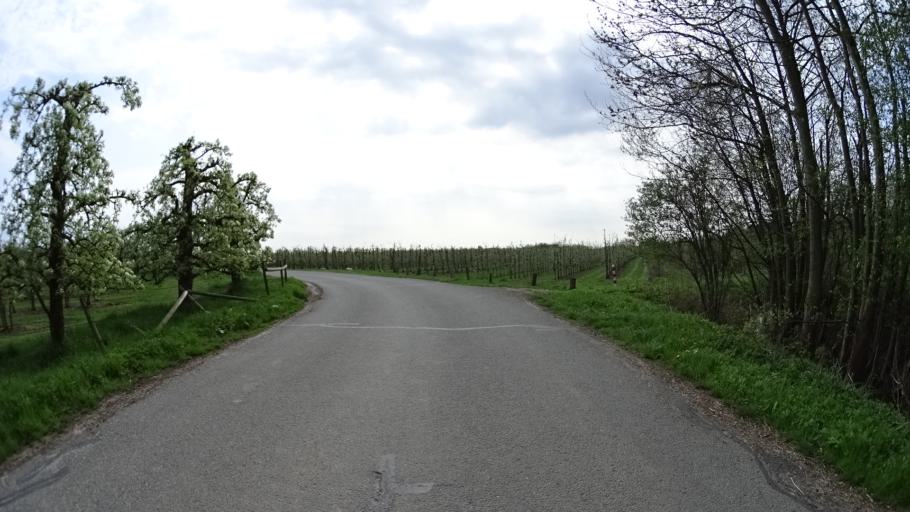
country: DE
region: Schleswig-Holstein
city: Wedel
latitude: 53.5425
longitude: 9.7413
